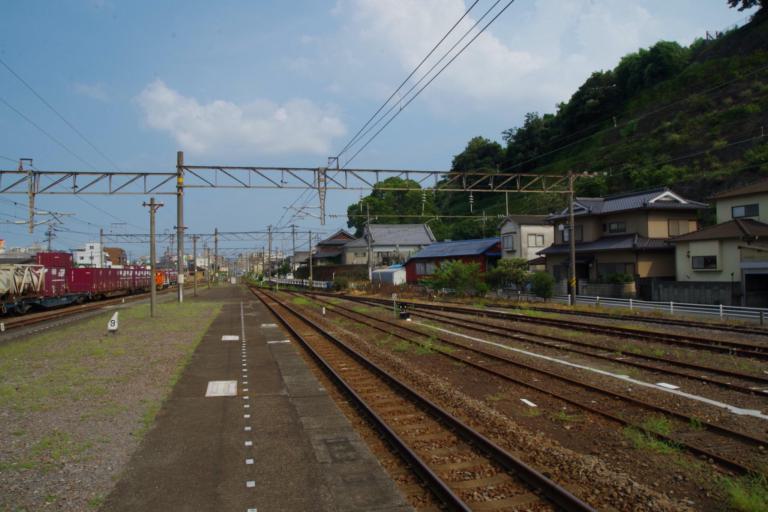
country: JP
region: Oita
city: Oita
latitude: 33.2445
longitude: 131.5837
